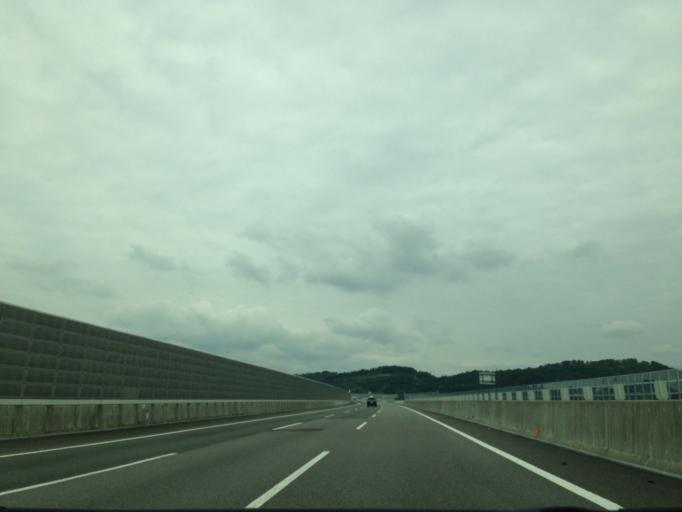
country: JP
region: Shizuoka
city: Hamakita
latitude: 34.8370
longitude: 137.8043
